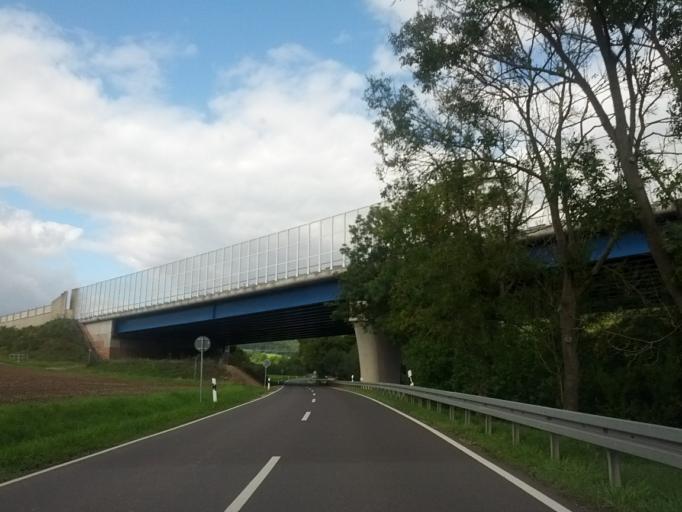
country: DE
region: Hesse
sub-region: Regierungsbezirk Kassel
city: Herleshausen
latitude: 51.0101
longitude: 10.1605
